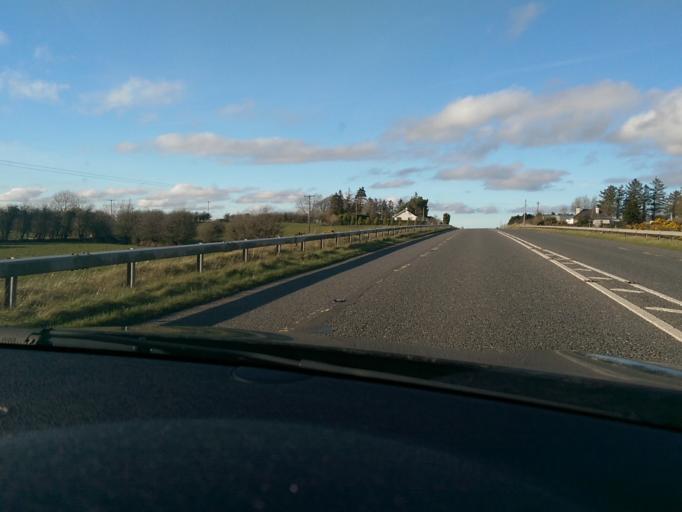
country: IE
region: Connaught
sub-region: Roscommon
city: Roscommon
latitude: 53.6673
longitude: -8.1979
